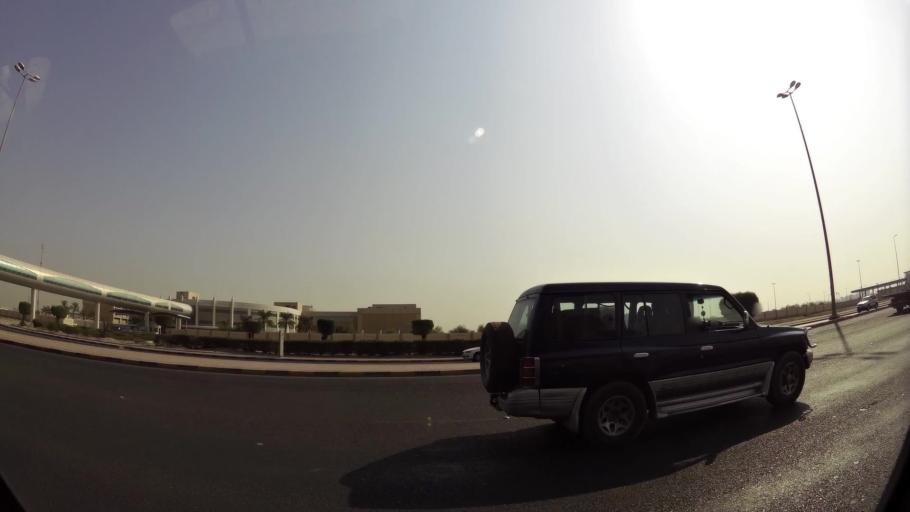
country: KW
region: Al Asimah
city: Ar Rabiyah
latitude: 29.2754
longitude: 47.9071
